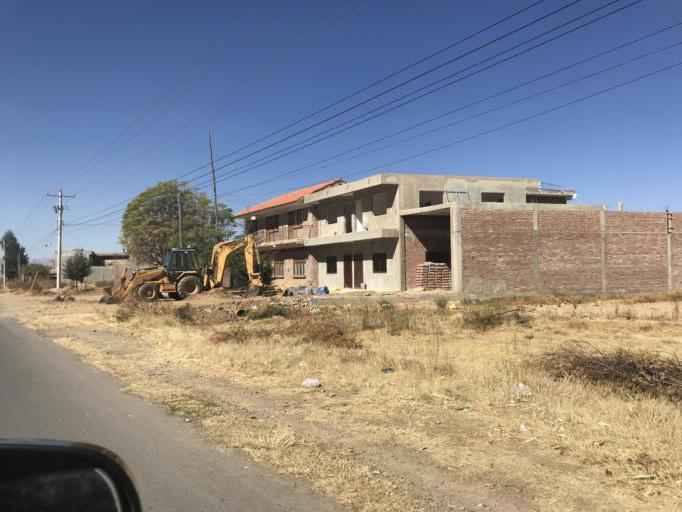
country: BO
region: Cochabamba
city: Tarata
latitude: -17.6022
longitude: -65.9768
